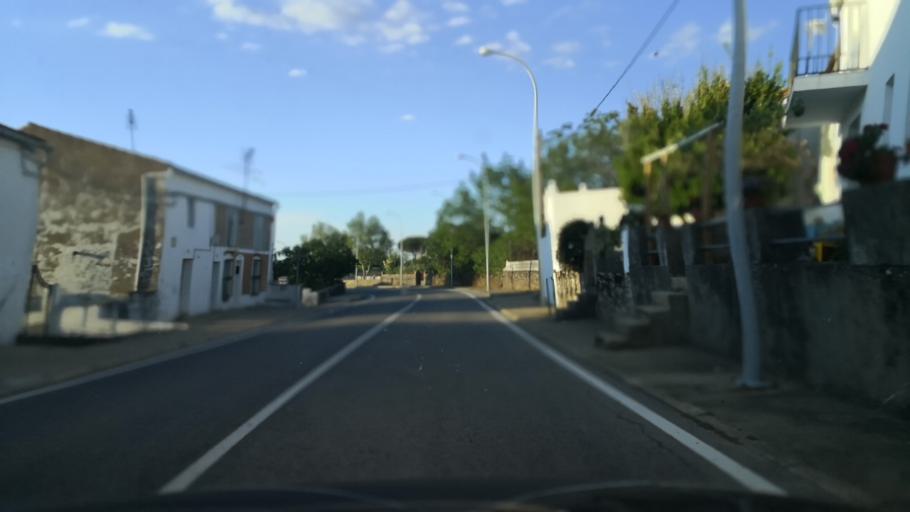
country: PT
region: Portalegre
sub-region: Portalegre
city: Sao Juliao
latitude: 39.3494
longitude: -7.2751
